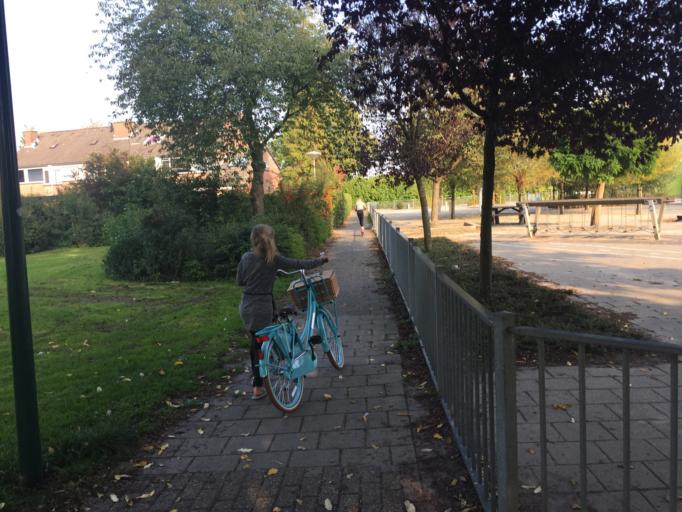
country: NL
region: Utrecht
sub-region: Gemeente Montfoort
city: Montfoort
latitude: 52.0402
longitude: 4.9508
